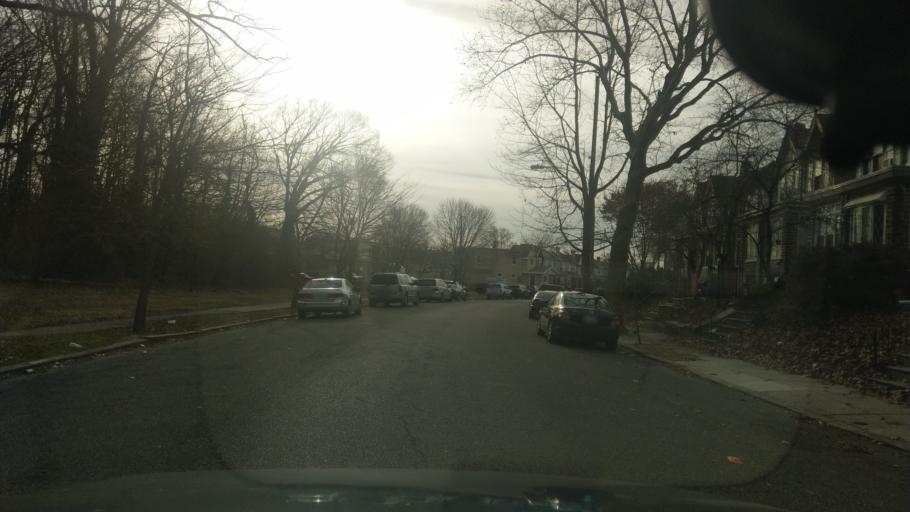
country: US
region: Pennsylvania
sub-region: Montgomery County
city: Jenkintown
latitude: 40.0428
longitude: -75.1332
